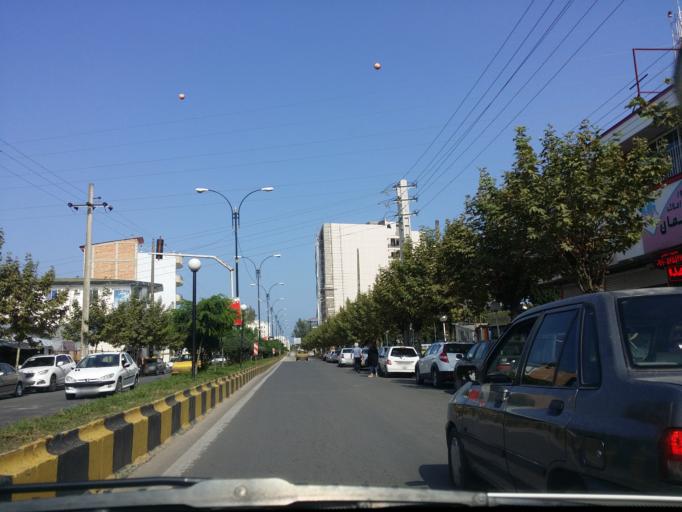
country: IR
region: Mazandaran
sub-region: Nowshahr
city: Nowshahr
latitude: 36.6441
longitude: 51.4916
